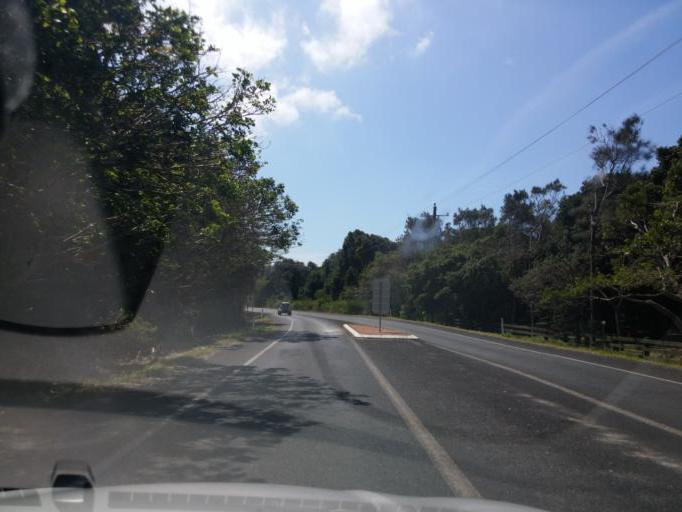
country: AU
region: New South Wales
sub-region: Great Lakes
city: Forster
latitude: -32.3036
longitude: 152.5204
